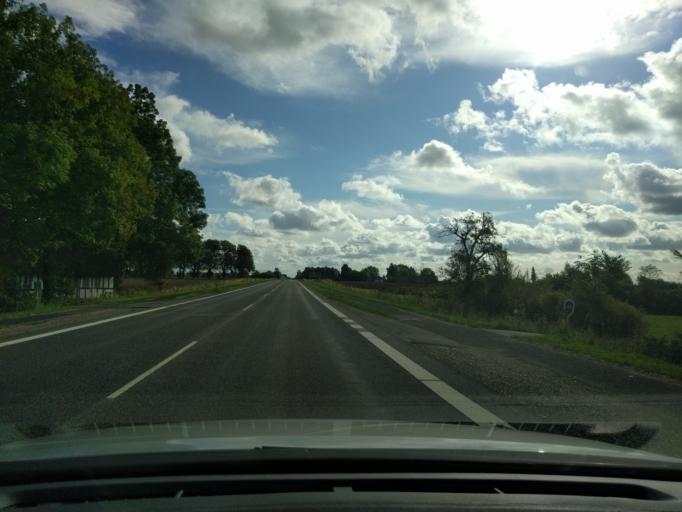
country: DK
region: South Denmark
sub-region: Nyborg Kommune
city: Ullerslev
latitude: 55.3626
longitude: 10.6256
